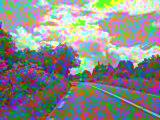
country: IE
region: Ulster
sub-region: County Donegal
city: Ballybofey
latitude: 54.8216
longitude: -7.7547
